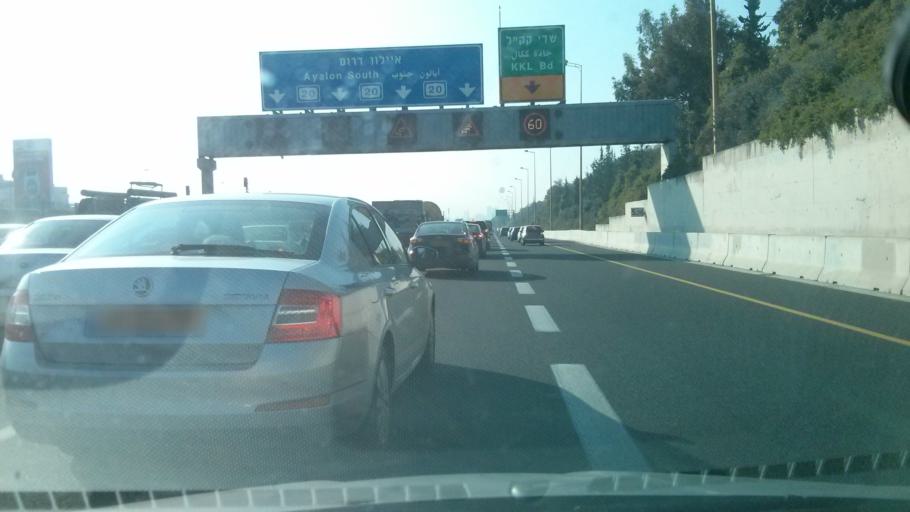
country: IL
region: Tel Aviv
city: Ramat HaSharon
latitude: 32.1267
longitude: 34.8099
